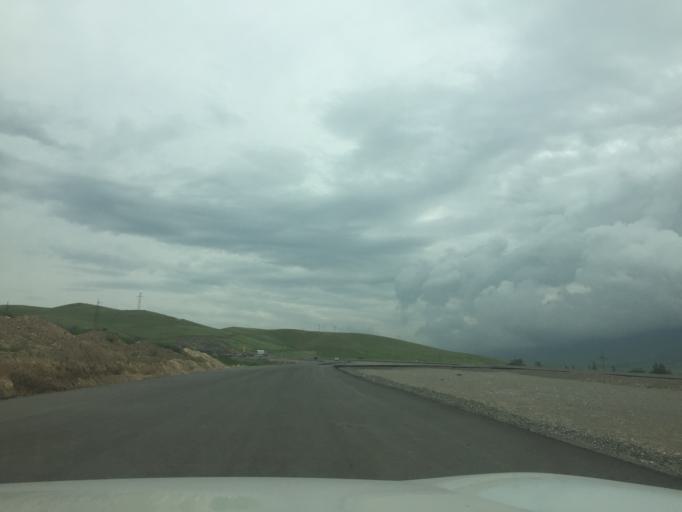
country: KZ
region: Ongtustik Qazaqstan
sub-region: Tulkibas Audany
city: Zhabagly
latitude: 42.5172
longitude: 70.5567
